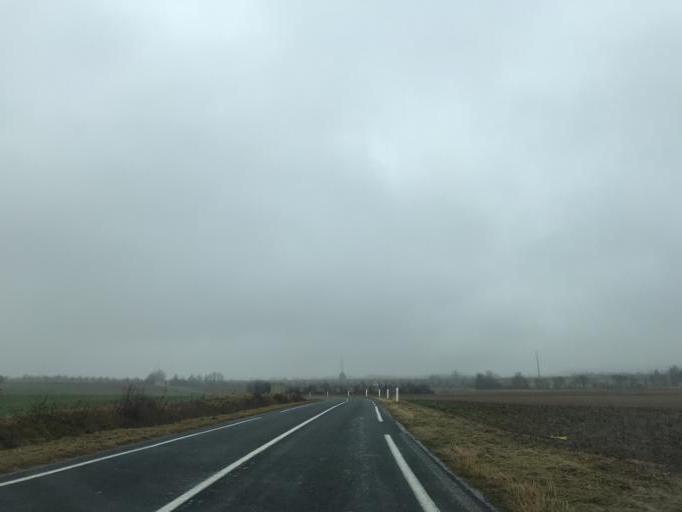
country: FR
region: Rhone-Alpes
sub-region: Departement de l'Ain
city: Mionnay
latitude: 45.8656
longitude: 4.9195
